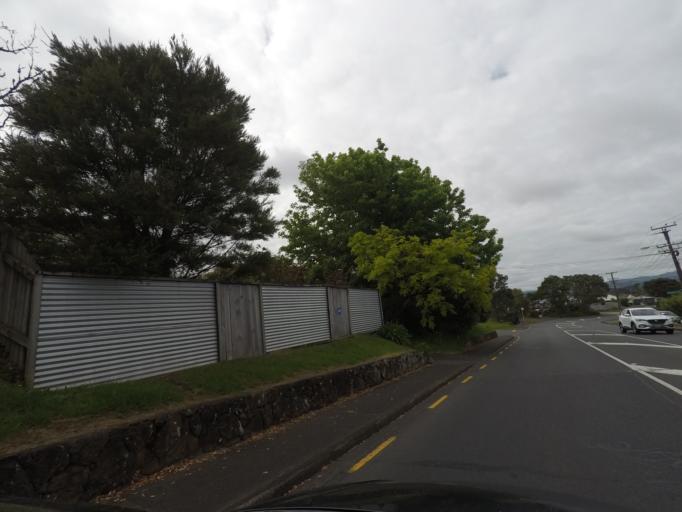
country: NZ
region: Auckland
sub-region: Auckland
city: Rosebank
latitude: -36.8453
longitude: 174.6080
